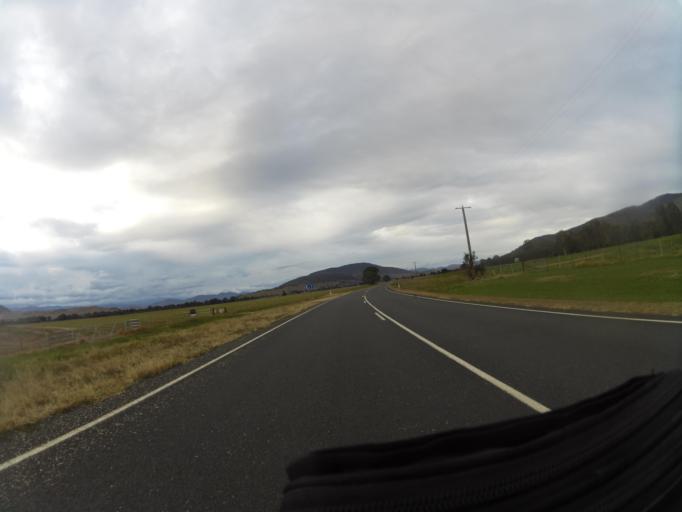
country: AU
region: New South Wales
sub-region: Snowy River
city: Jindabyne
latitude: -36.0941
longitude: 147.9822
